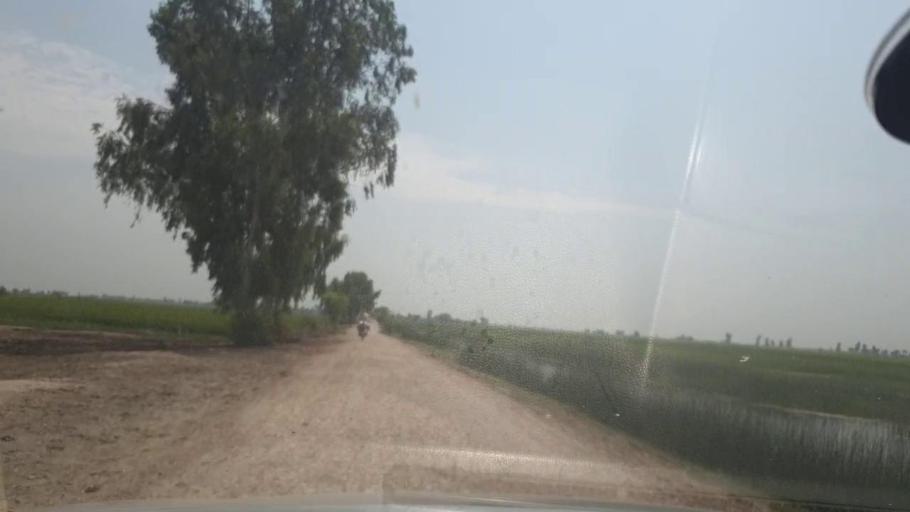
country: PK
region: Sindh
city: Thul
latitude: 28.1675
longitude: 68.6486
